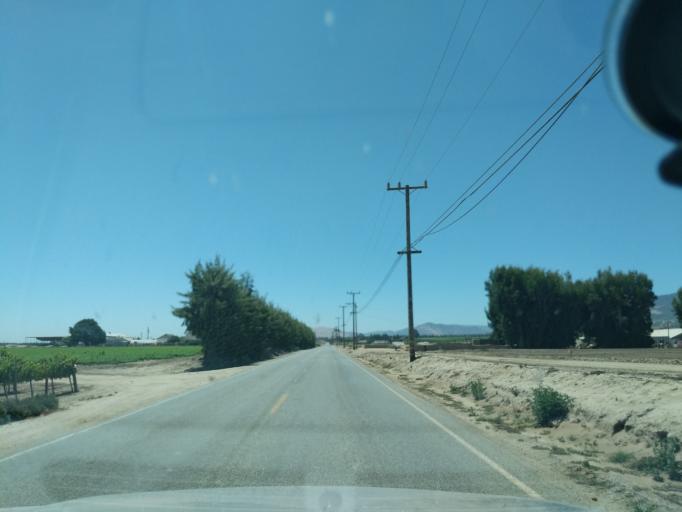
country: US
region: California
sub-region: Monterey County
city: Soledad
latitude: 36.3850
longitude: -121.3306
